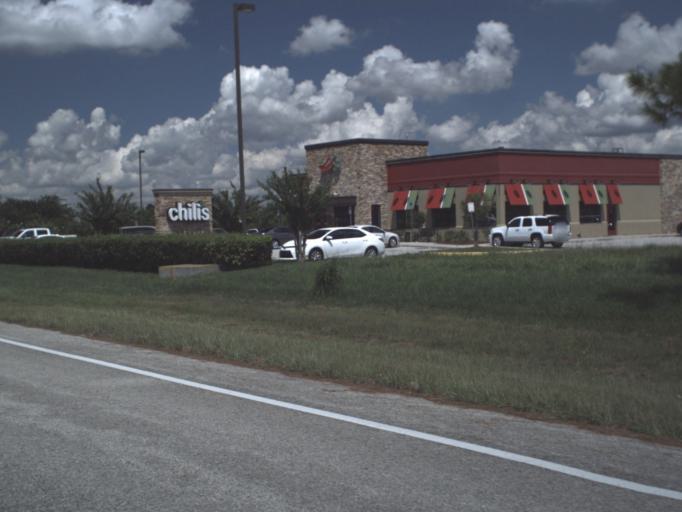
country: US
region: Florida
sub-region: Polk County
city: Lake Wales
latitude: 27.9532
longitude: -81.6198
